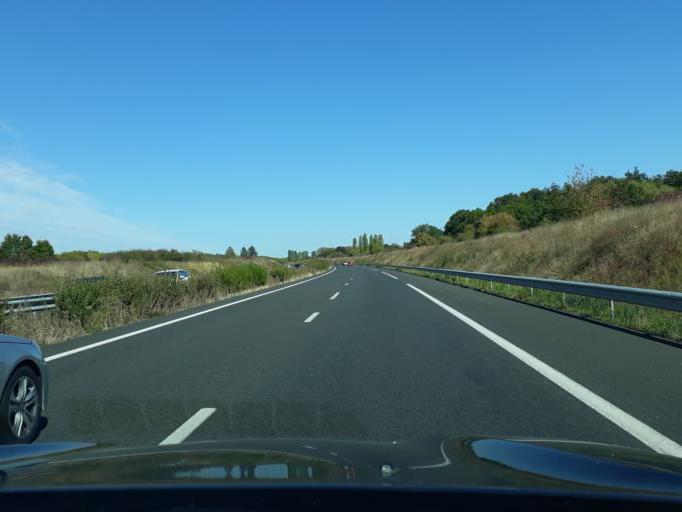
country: FR
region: Centre
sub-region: Departement d'Indre-et-Loire
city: Ballan-Mire
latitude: 47.3212
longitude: 0.5997
